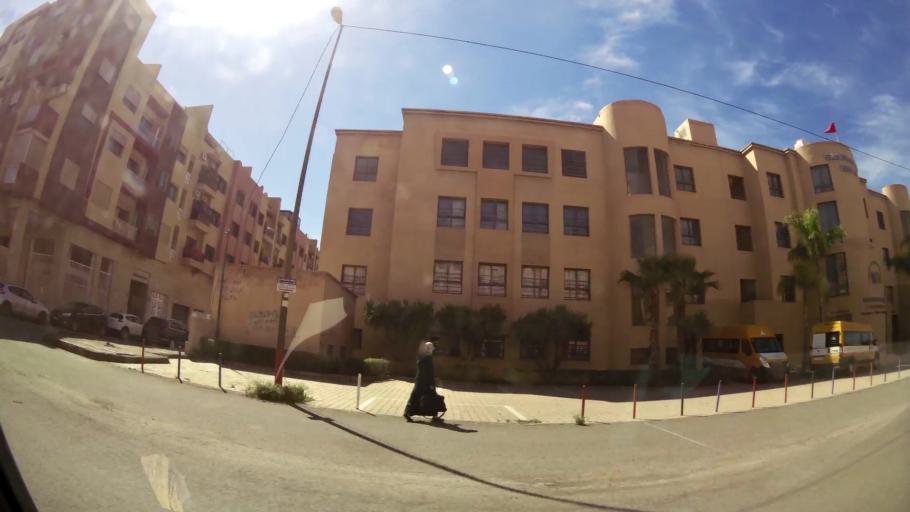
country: MA
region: Marrakech-Tensift-Al Haouz
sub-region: Marrakech
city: Marrakesh
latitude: 31.6784
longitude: -8.0257
